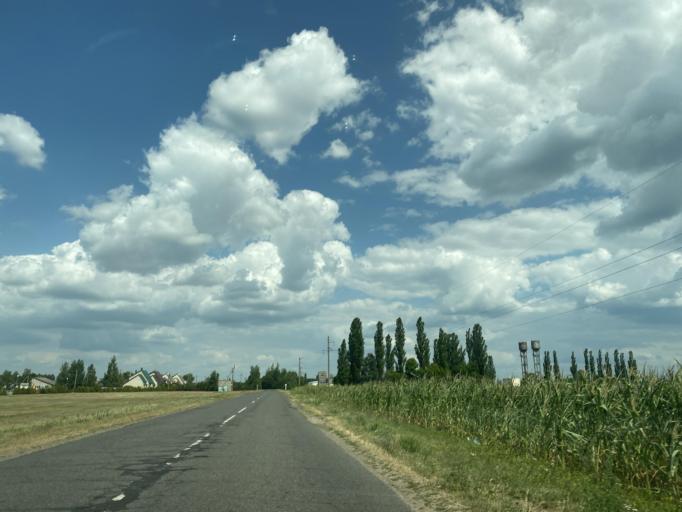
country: BY
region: Brest
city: Ivanava
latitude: 52.3454
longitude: 25.6275
